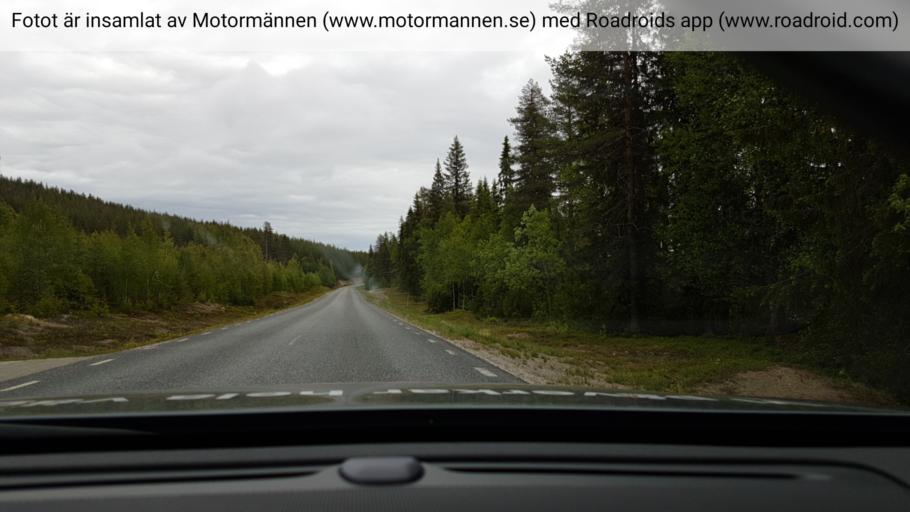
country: SE
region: Vaesterbotten
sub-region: Asele Kommun
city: Insjon
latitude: 64.3501
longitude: 17.8300
